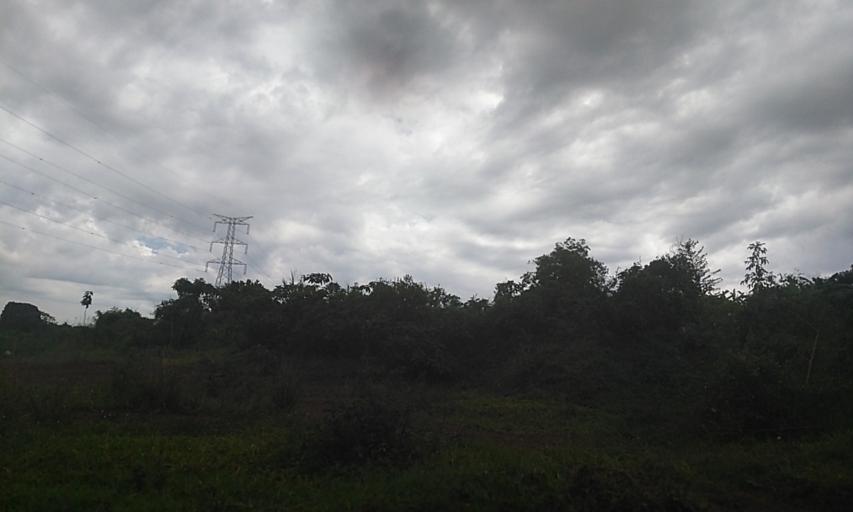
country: UG
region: Central Region
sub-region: Wakiso District
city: Kireka
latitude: 0.4059
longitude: 32.6305
